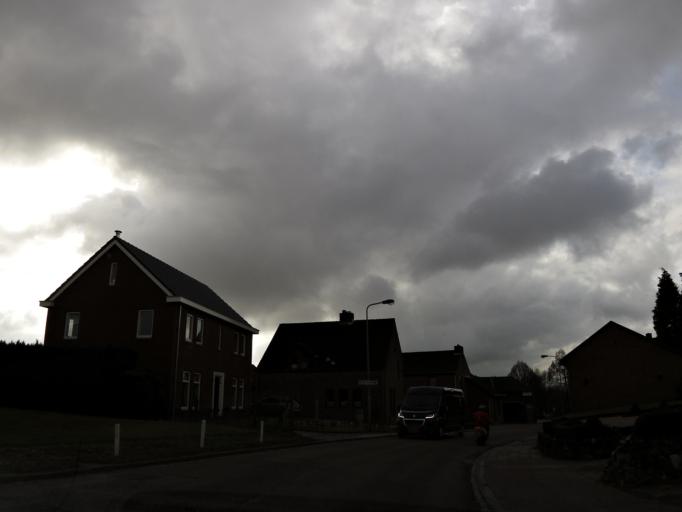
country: NL
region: Limburg
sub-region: Eijsden-Margraten
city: Eijsden
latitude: 50.7968
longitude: 5.7652
